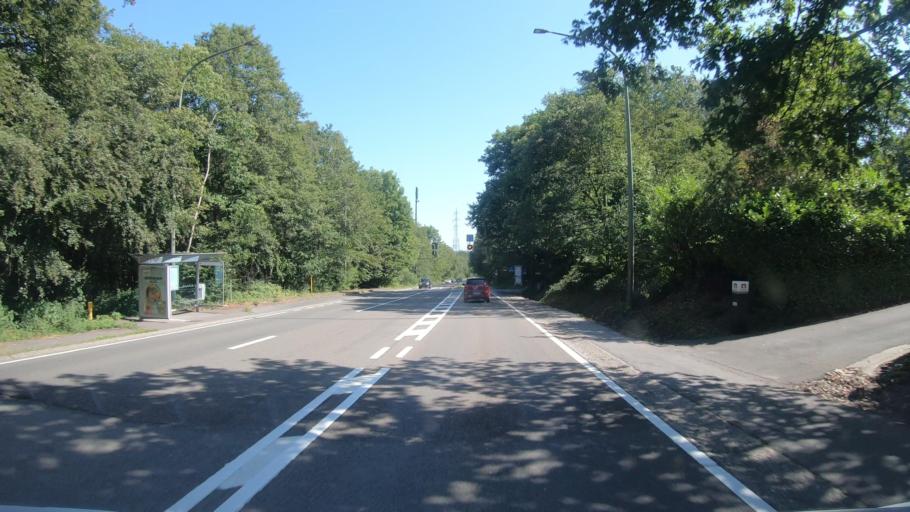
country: BE
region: Wallonia
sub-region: Province de Liege
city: Liege
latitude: 50.6047
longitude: 5.5851
